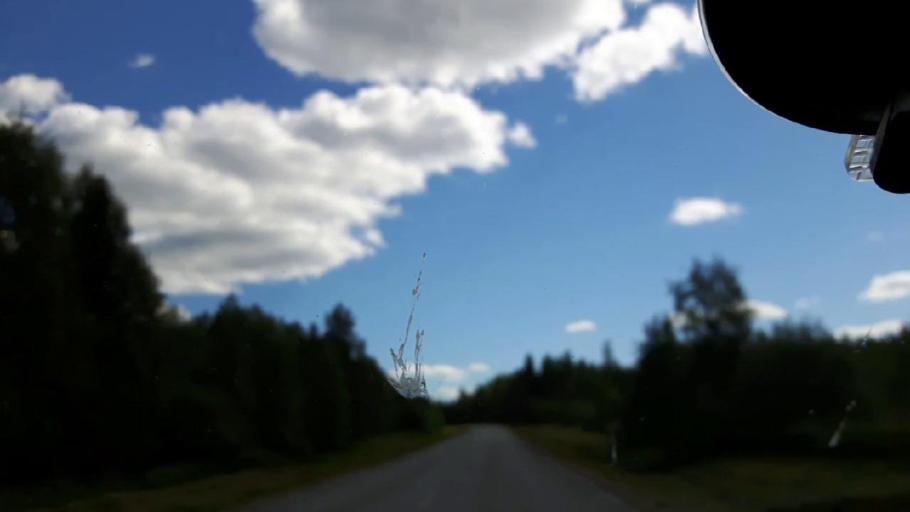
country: SE
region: Jaemtland
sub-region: Ragunda Kommun
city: Hammarstrand
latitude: 62.8286
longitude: 16.1861
